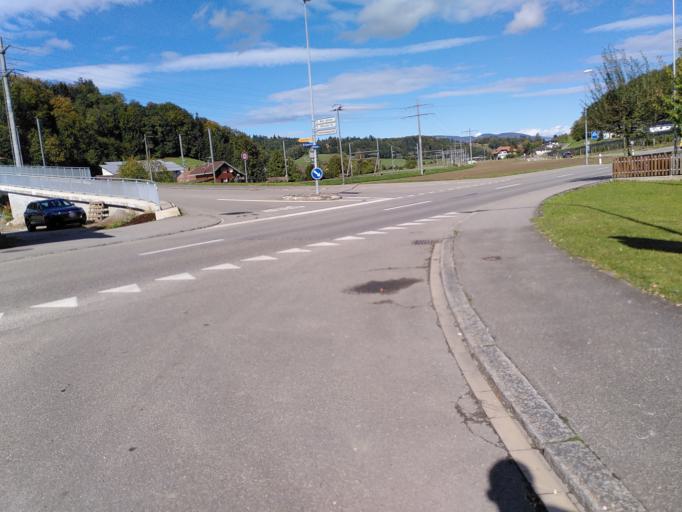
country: CH
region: Bern
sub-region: Oberaargau
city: Seeberg
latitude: 47.1420
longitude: 7.6975
